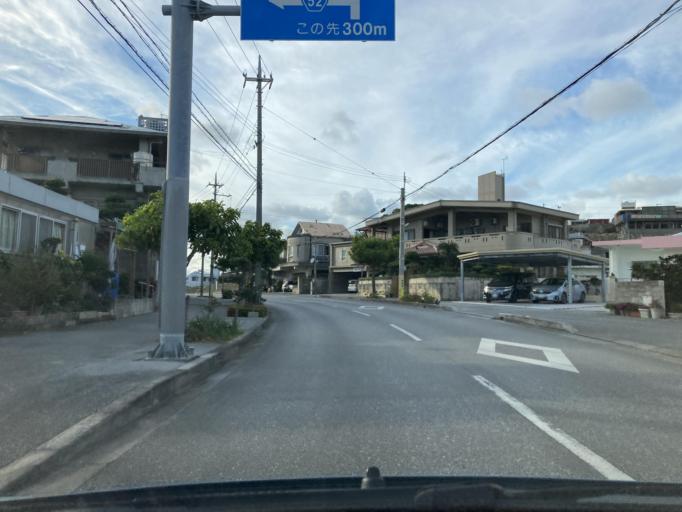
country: JP
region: Okinawa
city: Itoman
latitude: 26.1382
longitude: 127.7413
